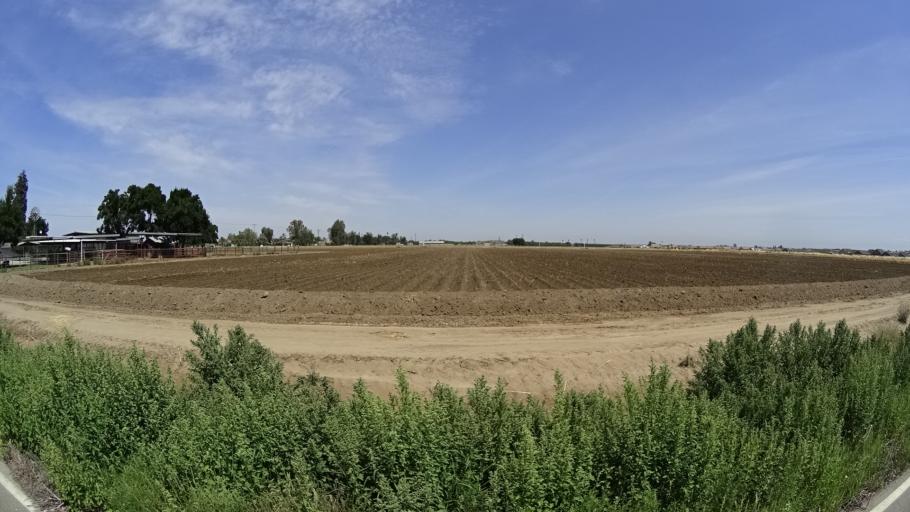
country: US
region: California
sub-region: Kings County
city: Armona
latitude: 36.3459
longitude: -119.6894
